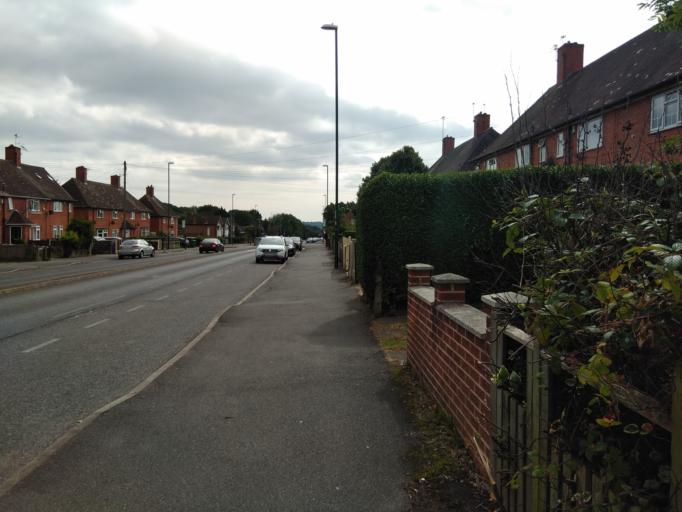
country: GB
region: England
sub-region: Nottinghamshire
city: Kimberley
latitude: 52.9695
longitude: -1.2123
